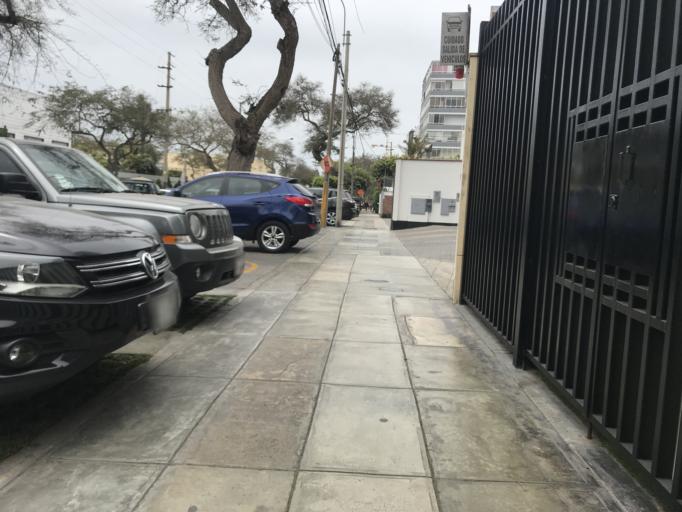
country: PE
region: Lima
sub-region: Lima
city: San Isidro
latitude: -12.1125
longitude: -77.0387
